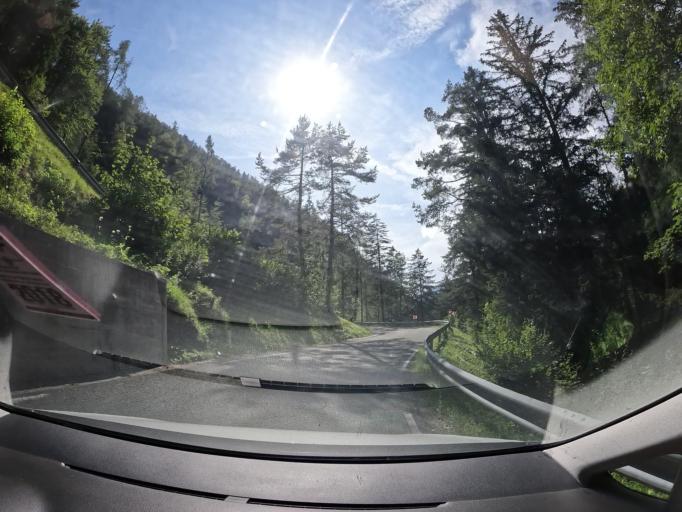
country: AT
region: Carinthia
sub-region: Politischer Bezirk Klagenfurt Land
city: Ludmannsdorf
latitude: 46.5204
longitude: 14.0969
